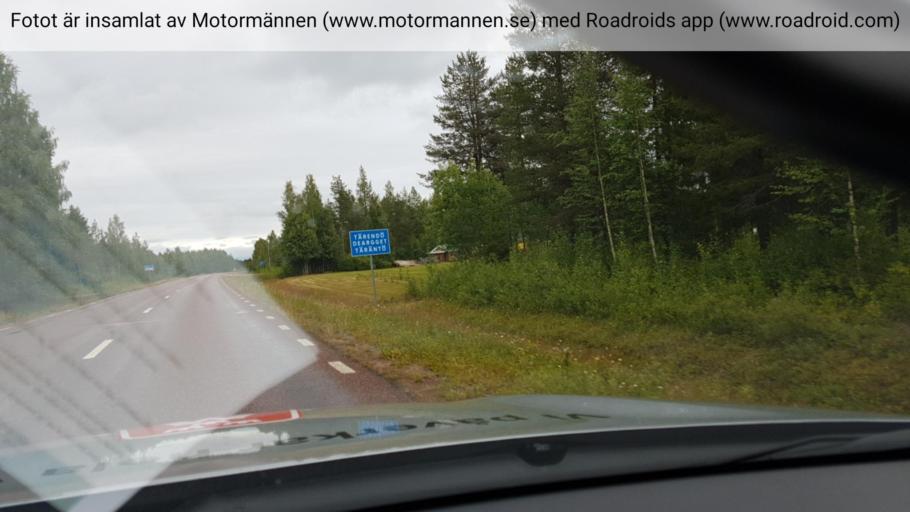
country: SE
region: Norrbotten
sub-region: Pajala Kommun
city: Pajala
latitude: 67.1359
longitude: 22.6110
